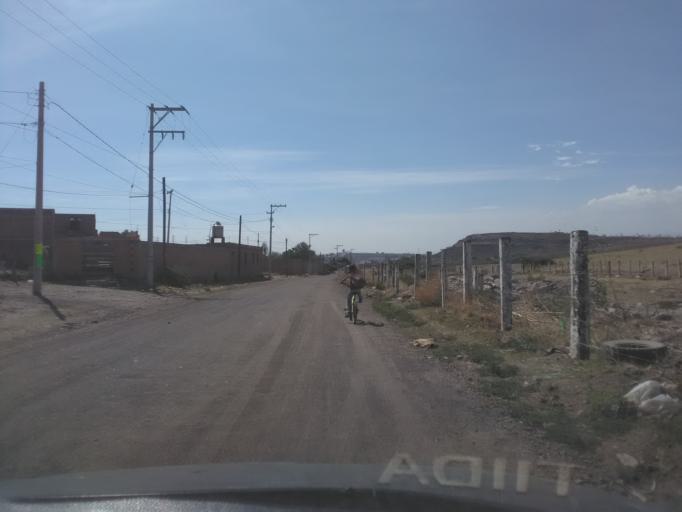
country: MX
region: Durango
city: Victoria de Durango
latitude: 24.0325
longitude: -104.7137
